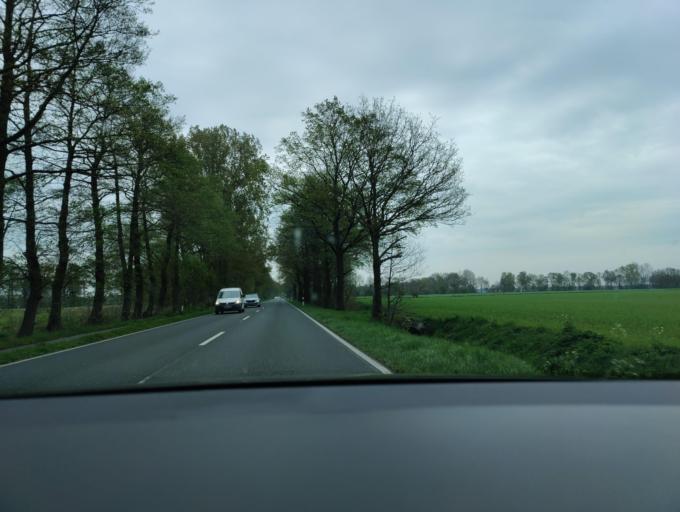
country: DE
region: Lower Saxony
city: Wietmarschen
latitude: 52.5372
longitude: 7.1495
